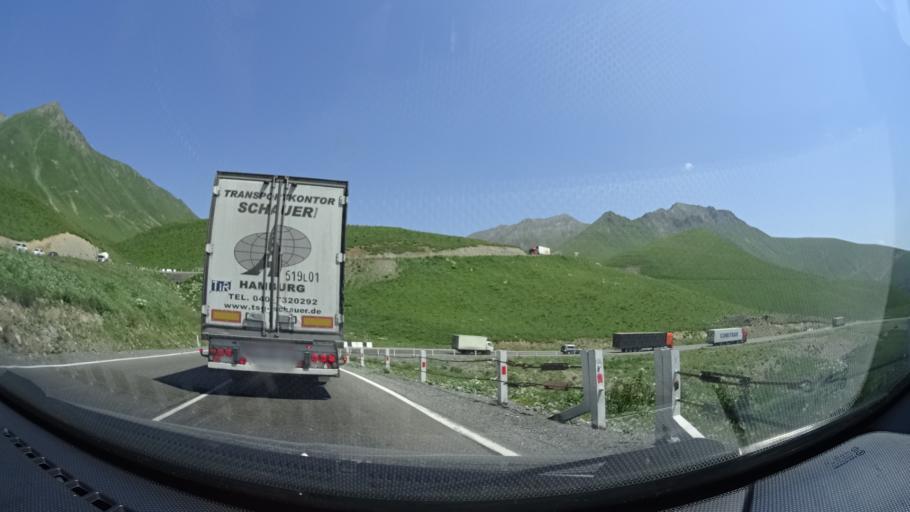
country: GE
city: Gudauri
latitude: 42.4980
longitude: 44.4466
